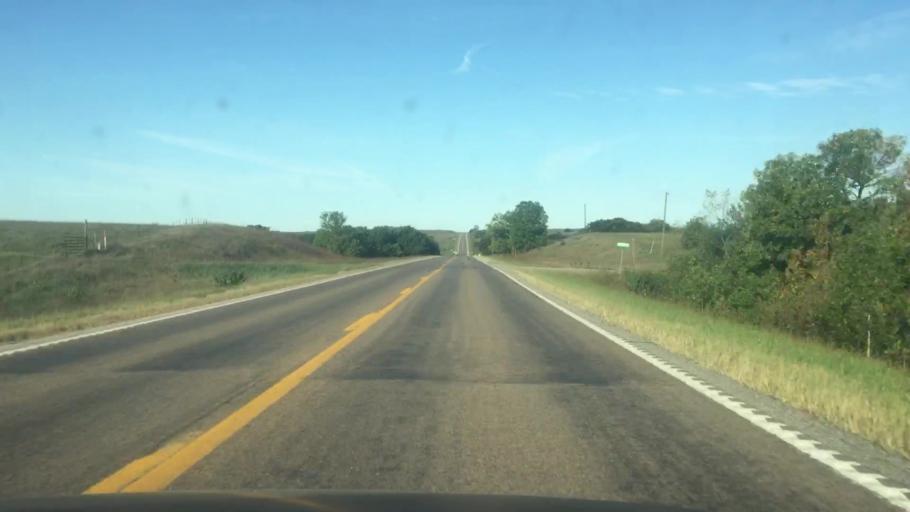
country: US
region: Nebraska
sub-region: Thayer County
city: Hebron
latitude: 40.1472
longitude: -97.5146
